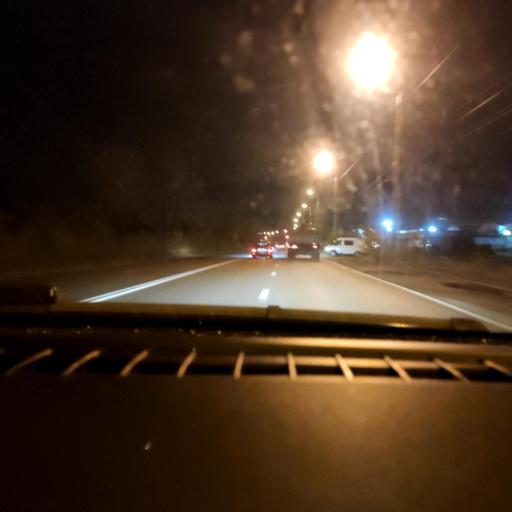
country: RU
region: Voronezj
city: Maslovka
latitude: 51.6111
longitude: 39.2569
